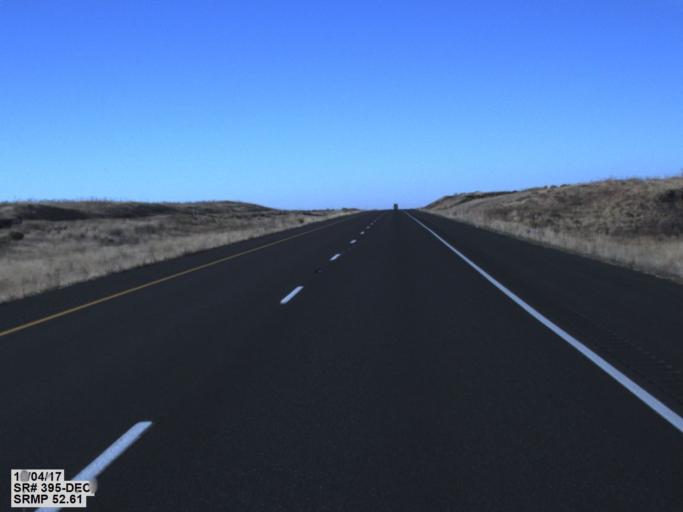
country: US
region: Washington
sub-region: Franklin County
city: Connell
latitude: 46.6283
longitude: -118.8851
